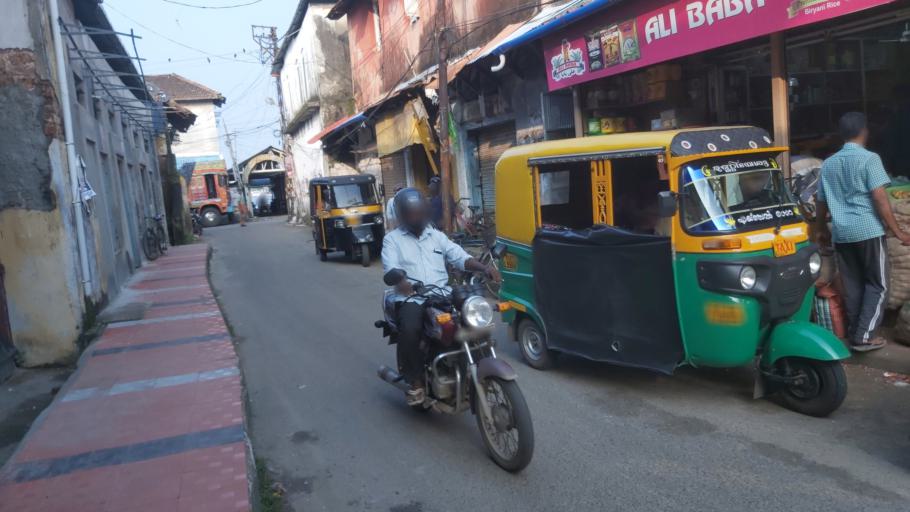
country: IN
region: Kerala
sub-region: Ernakulam
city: Cochin
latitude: 9.9647
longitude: 76.2549
